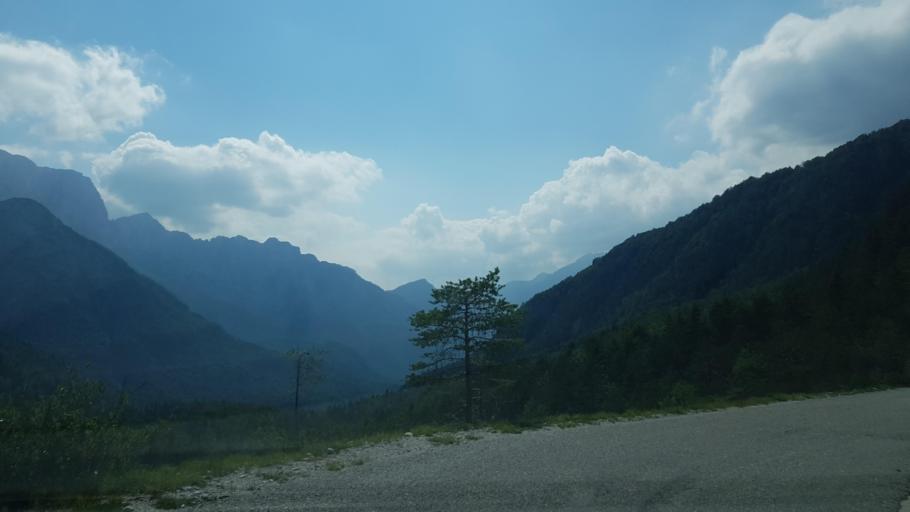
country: IT
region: Friuli Venezia Giulia
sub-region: Provincia di Udine
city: Malborghetto
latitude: 46.4625
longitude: 13.4266
